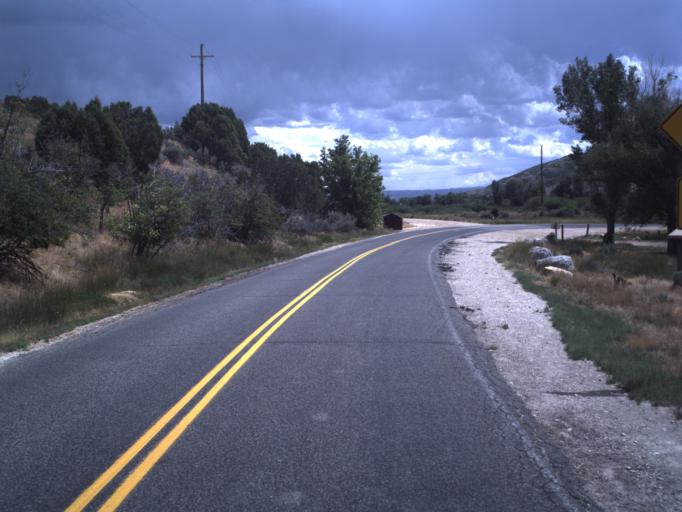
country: US
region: Utah
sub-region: Summit County
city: Oakley
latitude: 40.7547
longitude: -111.3718
